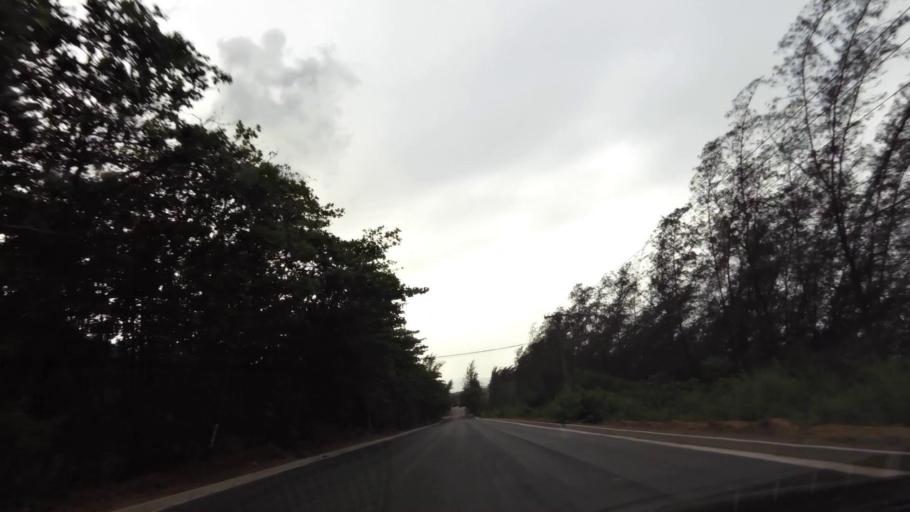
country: BR
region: Espirito Santo
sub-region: Guarapari
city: Guarapari
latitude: -20.7782
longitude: -40.5777
